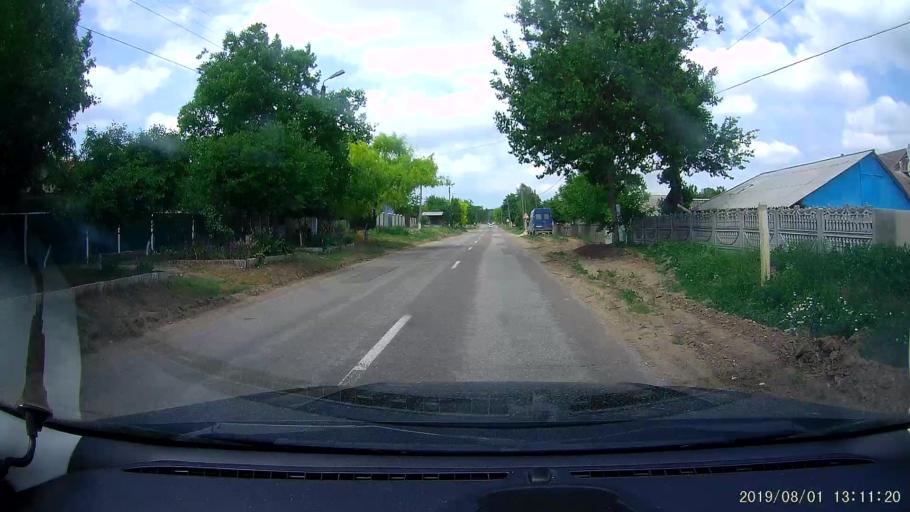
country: MD
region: Cahul
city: Cahul
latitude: 45.8495
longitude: 28.2981
